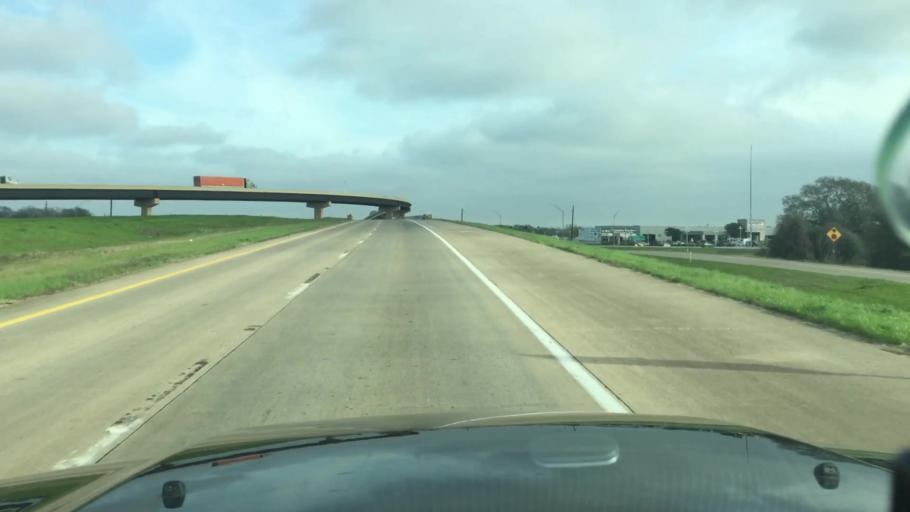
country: US
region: Texas
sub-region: Waller County
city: Hempstead
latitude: 30.1146
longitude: -96.0780
